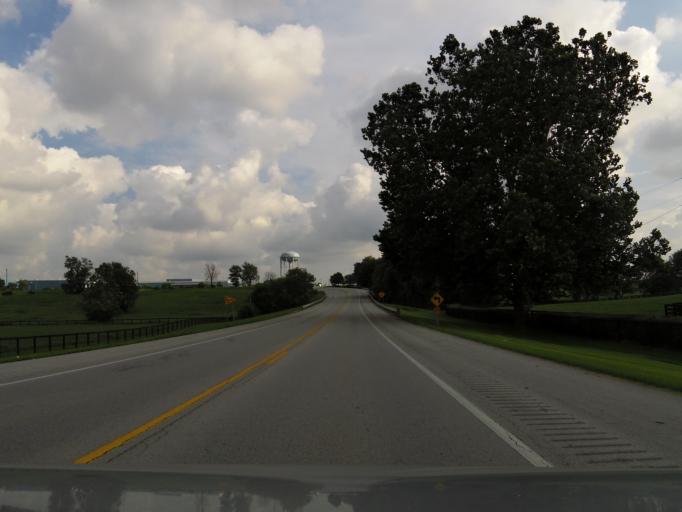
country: US
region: Kentucky
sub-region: Bourbon County
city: Paris
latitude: 38.2265
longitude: -84.2759
